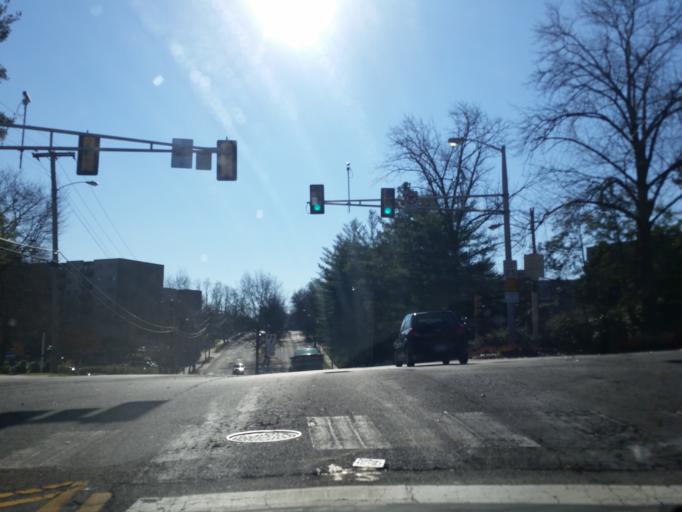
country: US
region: Virginia
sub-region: Fairfax County
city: Seven Corners
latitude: 38.8785
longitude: -77.1538
